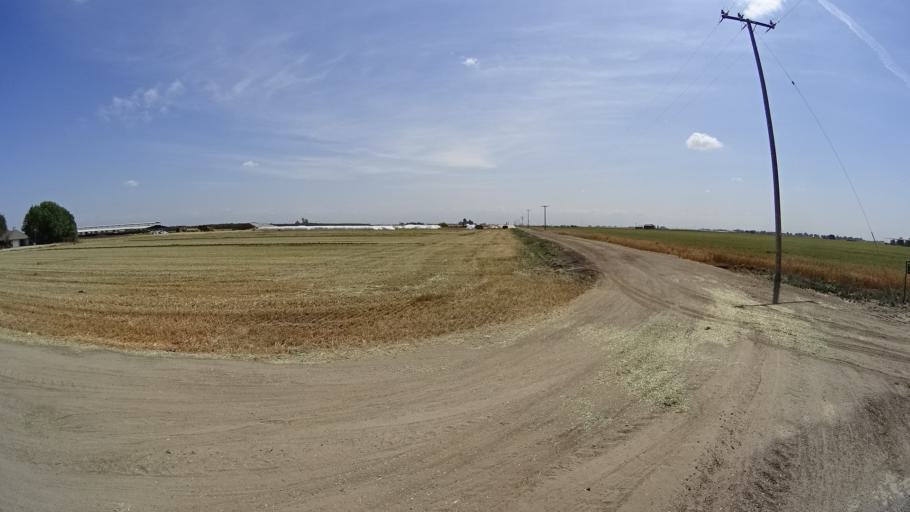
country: US
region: California
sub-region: Tulare County
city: Goshen
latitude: 36.3055
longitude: -119.4926
